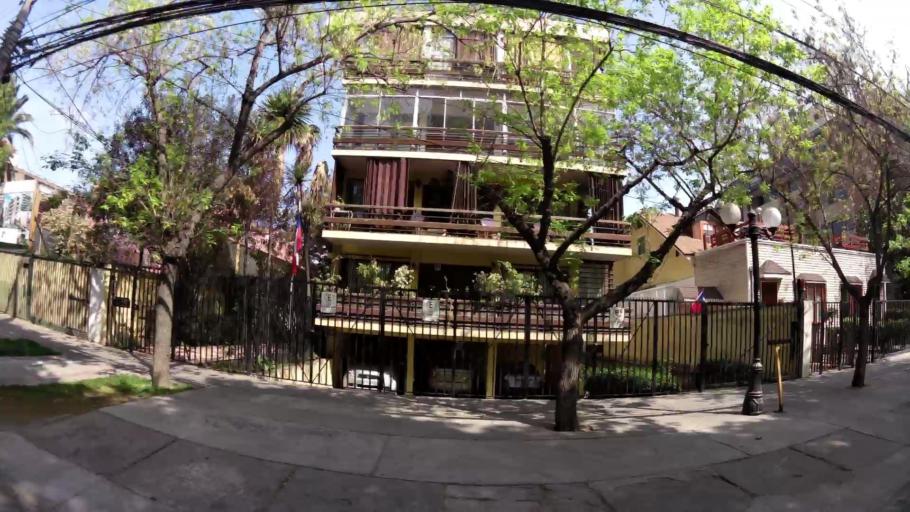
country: CL
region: Santiago Metropolitan
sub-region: Provincia de Santiago
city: Villa Presidente Frei, Nunoa, Santiago, Chile
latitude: -33.4262
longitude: -70.6061
